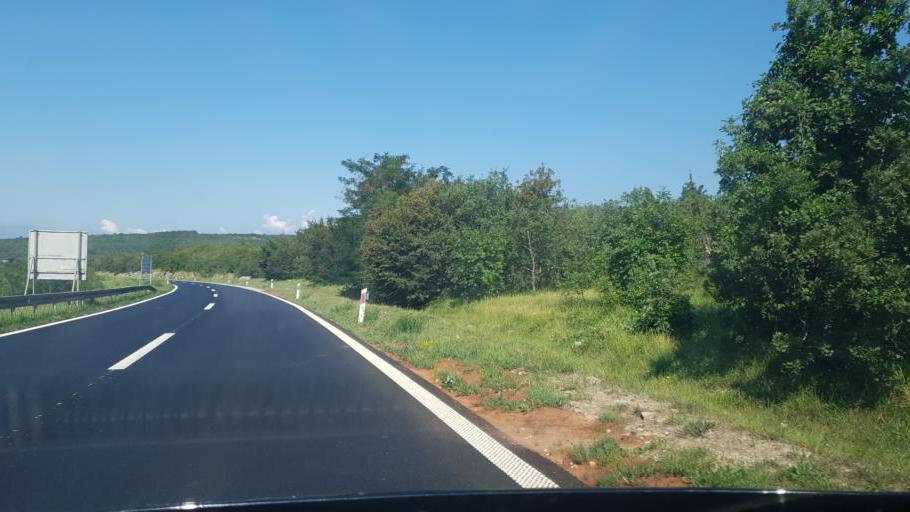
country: HR
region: Istarska
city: Buzet
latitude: 45.3506
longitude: 14.0979
